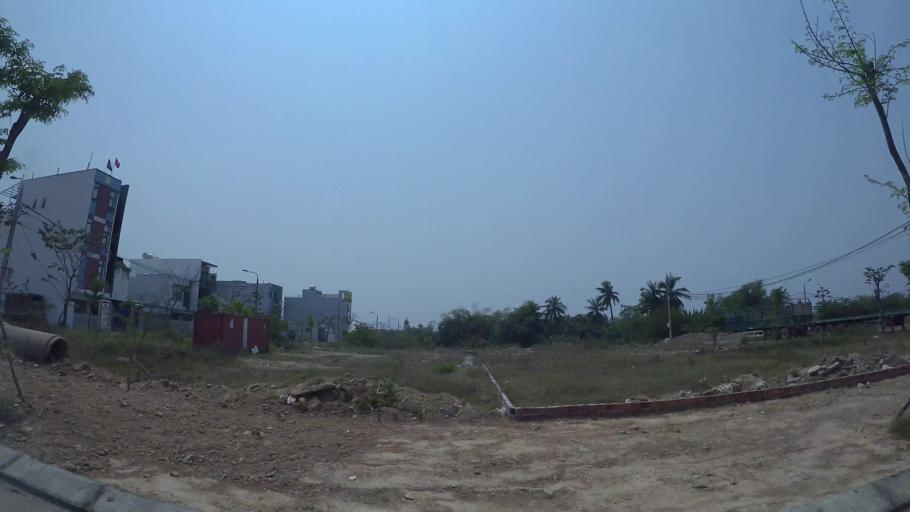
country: VN
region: Da Nang
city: Cam Le
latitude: 16.0185
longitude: 108.2275
